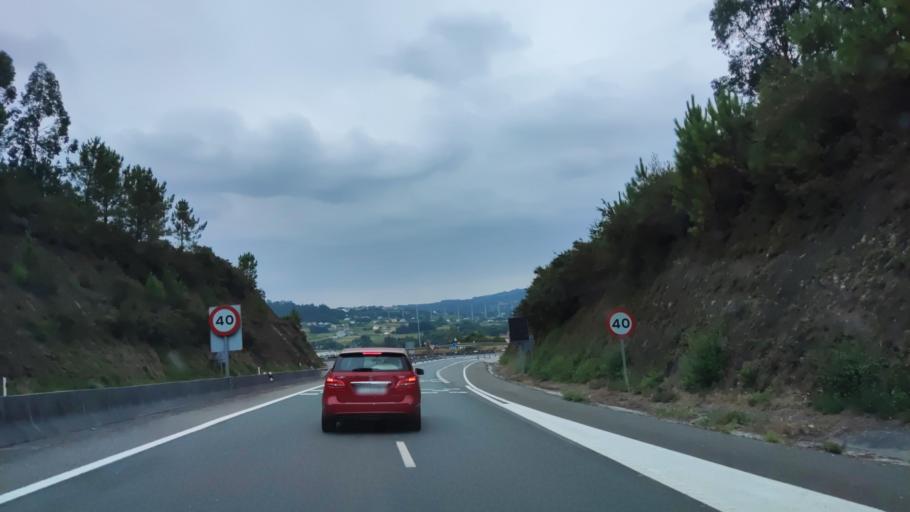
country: ES
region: Galicia
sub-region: Provincia da Coruna
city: Santiago de Compostela
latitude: 42.8361
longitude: -8.5291
